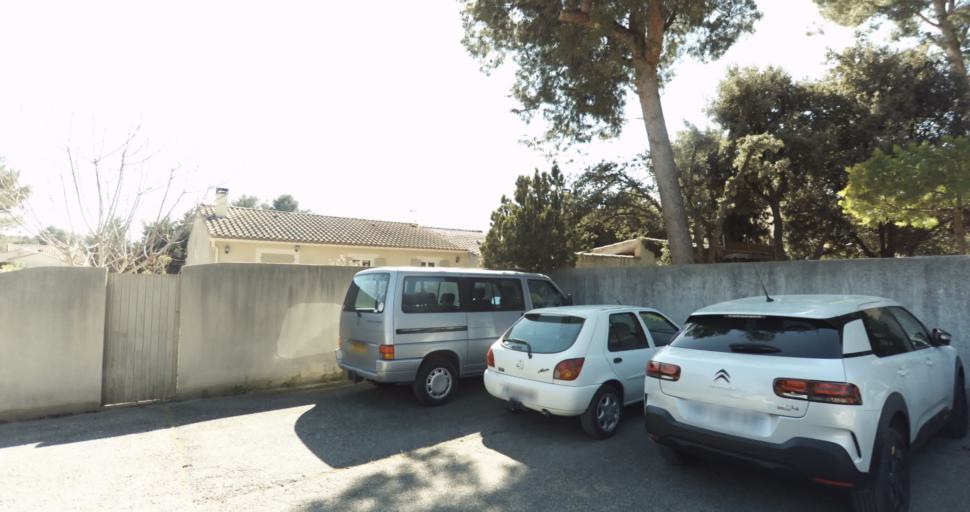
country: FR
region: Provence-Alpes-Cote d'Azur
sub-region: Departement des Bouches-du-Rhone
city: Pelissanne
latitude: 43.6386
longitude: 5.1598
